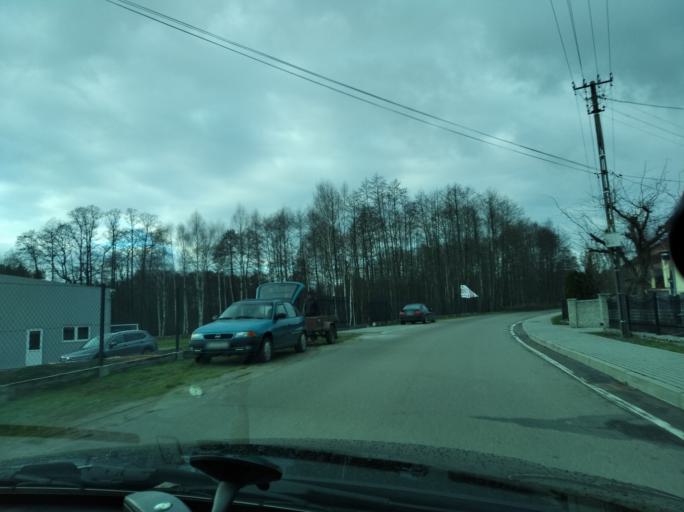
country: PL
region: Subcarpathian Voivodeship
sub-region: Powiat lancucki
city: Zolynia
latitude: 50.1454
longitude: 22.2768
